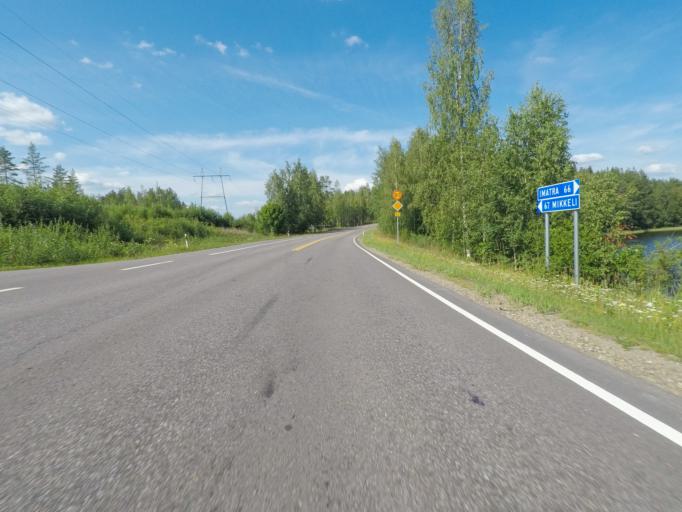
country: FI
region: Southern Savonia
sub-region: Mikkeli
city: Puumala
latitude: 61.5620
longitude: 28.1799
